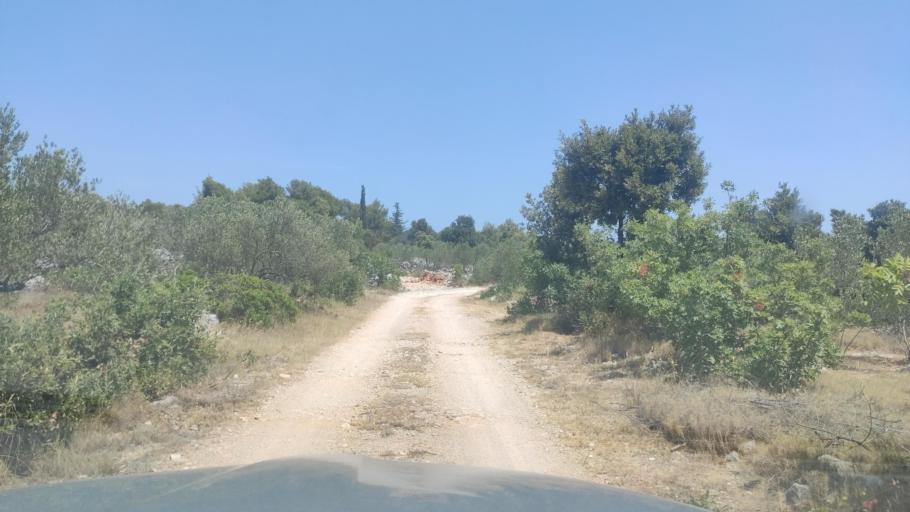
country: HR
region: Sibensko-Kniniska
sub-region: Grad Sibenik
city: Tisno
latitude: 43.7764
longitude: 15.6510
